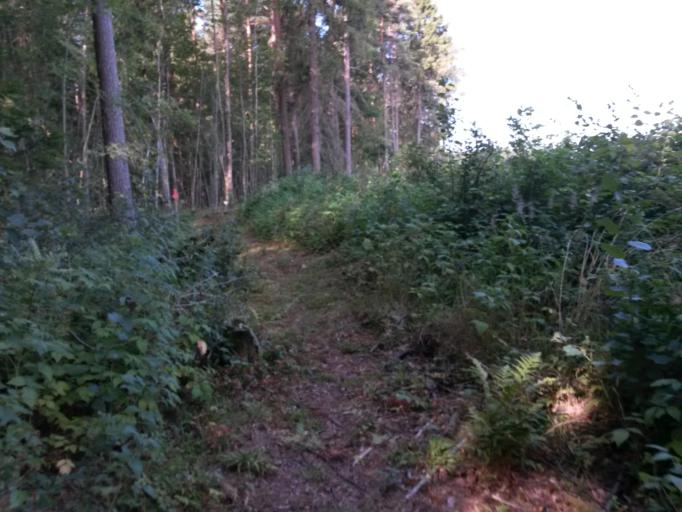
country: SE
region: Vaestra Goetaland
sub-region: Vargarda Kommun
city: Vargarda
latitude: 58.0479
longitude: 12.8222
